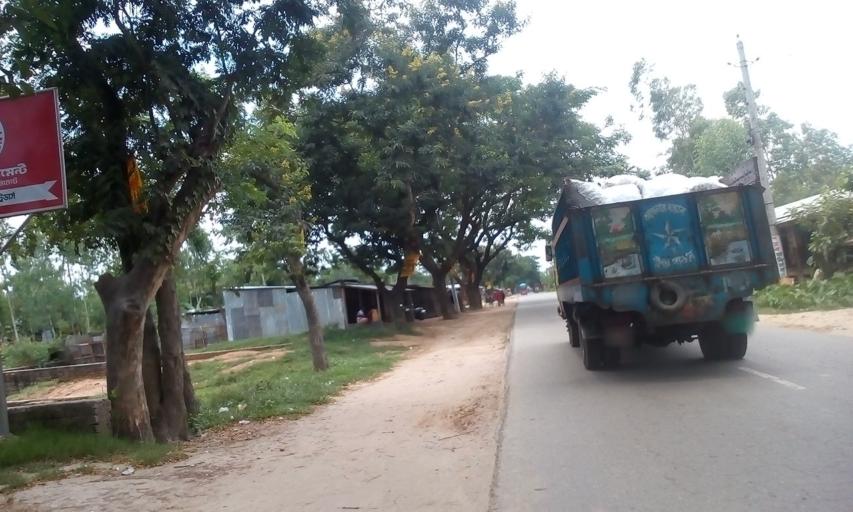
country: BD
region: Rangpur Division
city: Parbatipur
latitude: 25.3966
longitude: 88.9881
